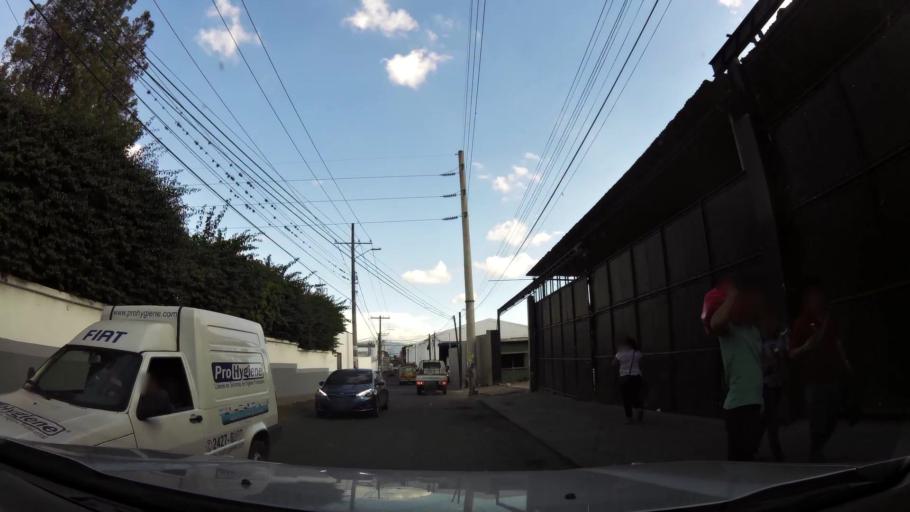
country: GT
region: Guatemala
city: Villa Nueva
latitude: 14.5294
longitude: -90.5896
